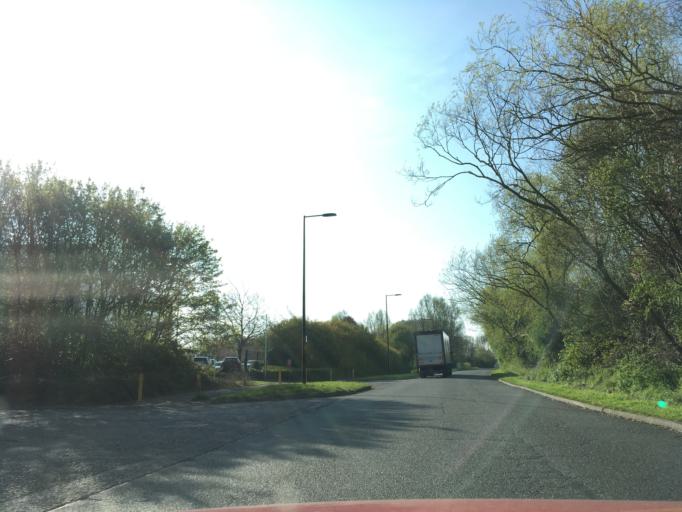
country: GB
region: England
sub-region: Milton Keynes
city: Newport Pagnell
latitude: 52.0669
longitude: -0.7284
